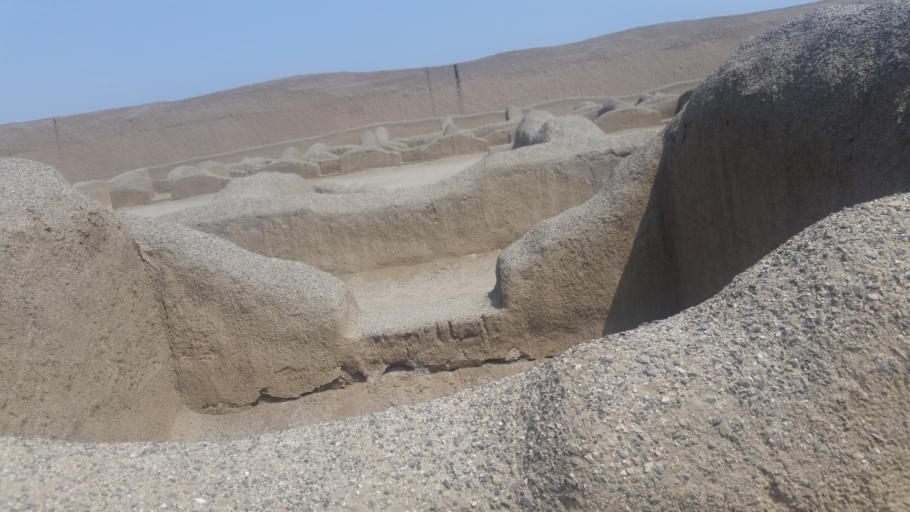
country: PE
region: La Libertad
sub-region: Provincia de Trujillo
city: Buenos Aires
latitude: -8.1112
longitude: -79.0740
